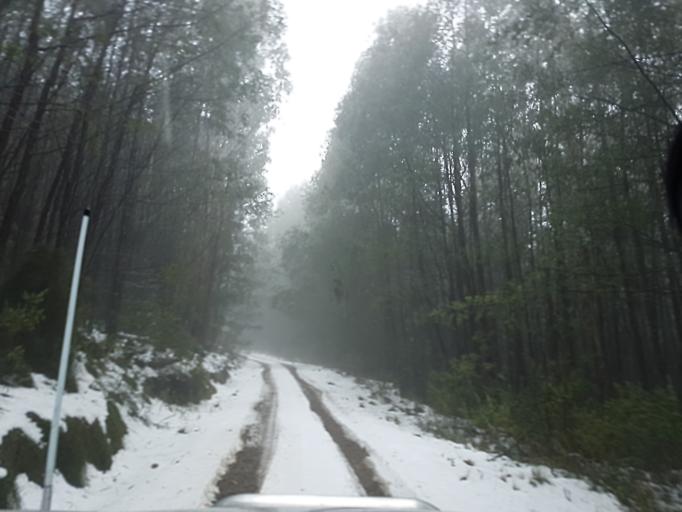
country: AU
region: Victoria
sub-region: Yarra Ranges
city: Millgrove
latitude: -37.5409
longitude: 145.8952
